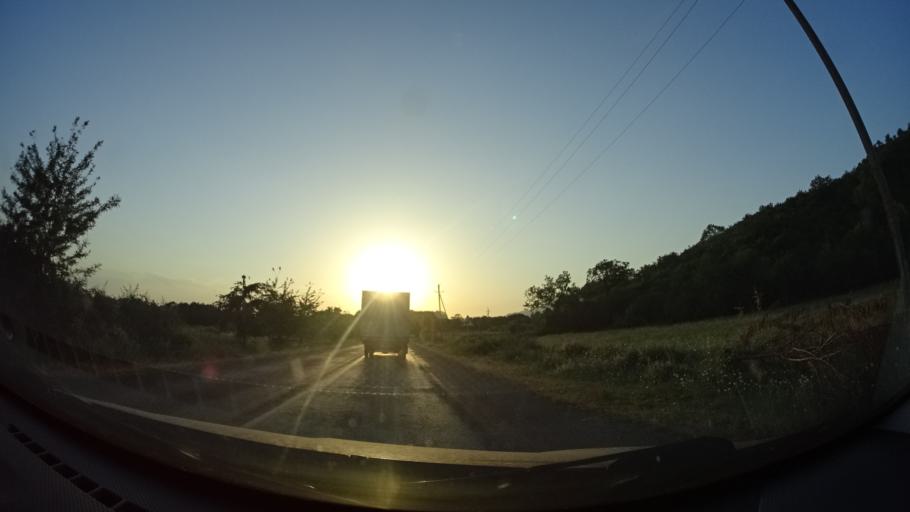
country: GE
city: Bagdadi
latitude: 41.8541
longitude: 46.0325
